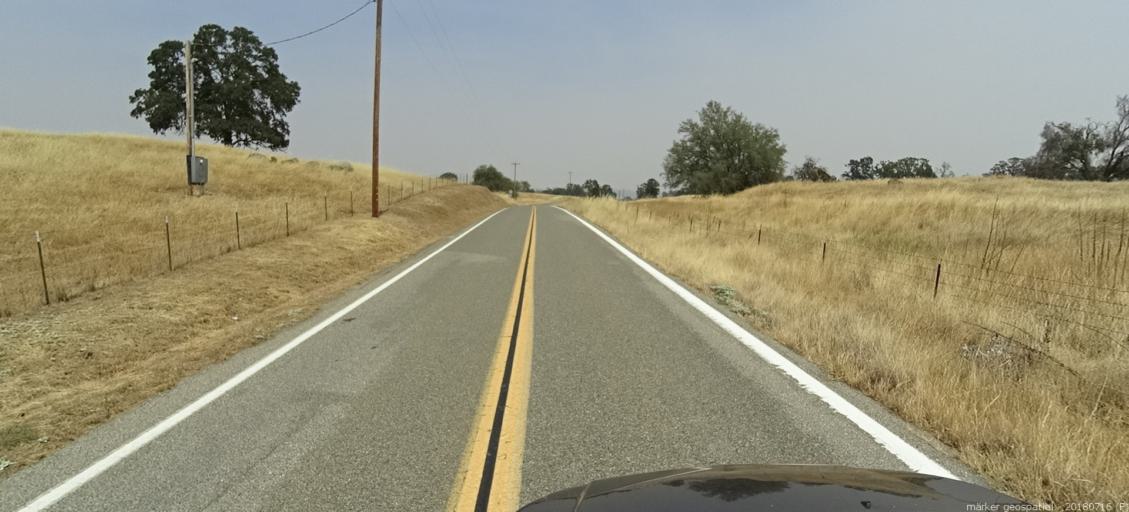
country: US
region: California
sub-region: Madera County
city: Yosemite Lakes
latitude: 37.1871
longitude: -119.9107
